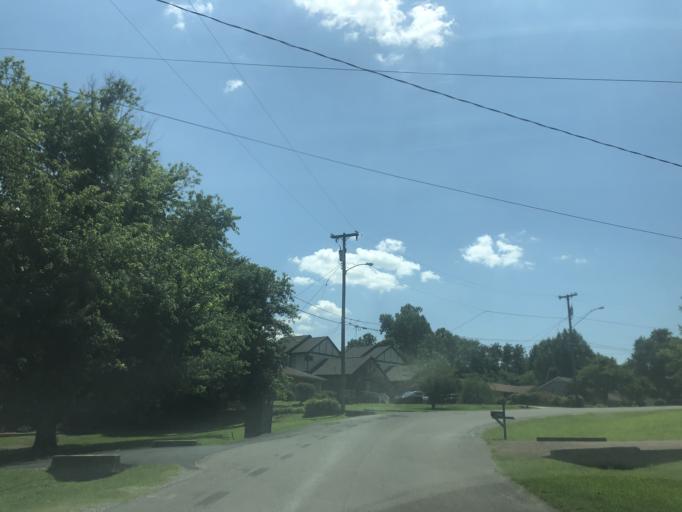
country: US
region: Tennessee
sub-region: Davidson County
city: Nashville
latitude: 36.1842
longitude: -86.7090
